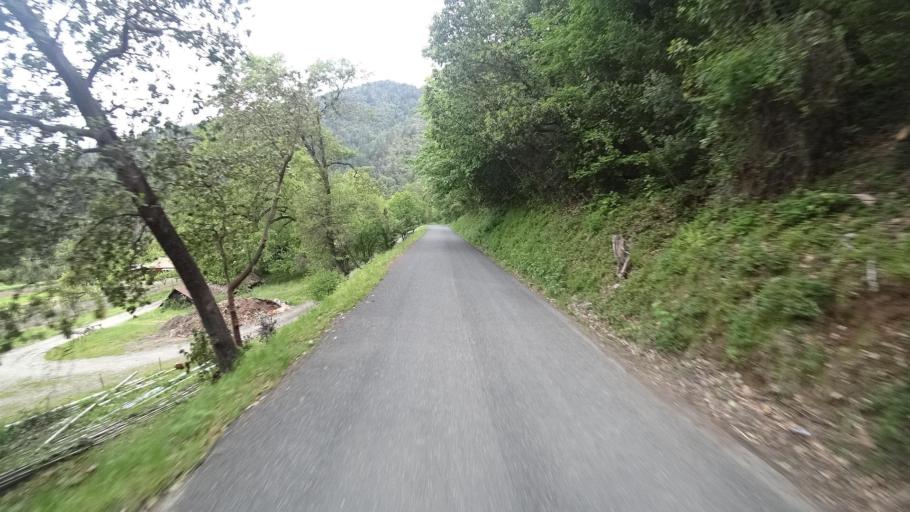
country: US
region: California
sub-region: Humboldt County
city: Willow Creek
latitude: 40.9430
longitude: -123.6118
